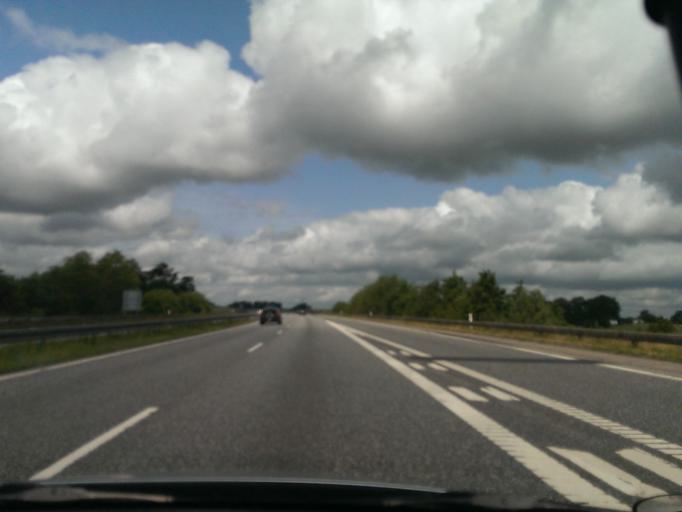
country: DK
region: North Denmark
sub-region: Mariagerfjord Kommune
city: Hobro
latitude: 56.5736
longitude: 9.8456
